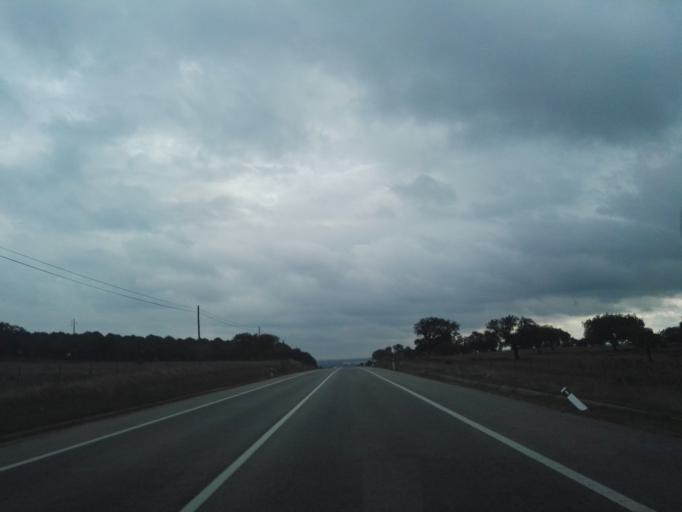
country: PT
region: Portalegre
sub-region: Arronches
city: Arronches
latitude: 39.1502
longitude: -7.3100
